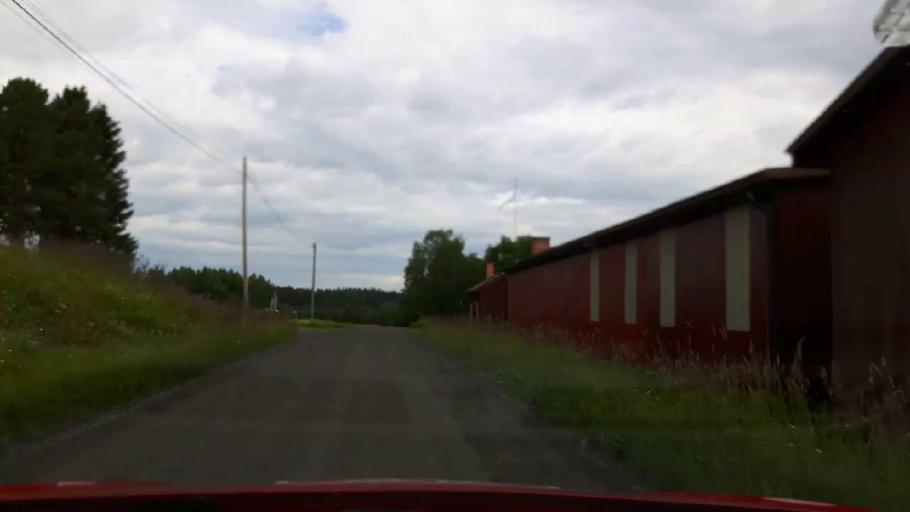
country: SE
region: Jaemtland
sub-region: Stroemsunds Kommun
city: Stroemsund
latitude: 63.4569
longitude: 15.2799
